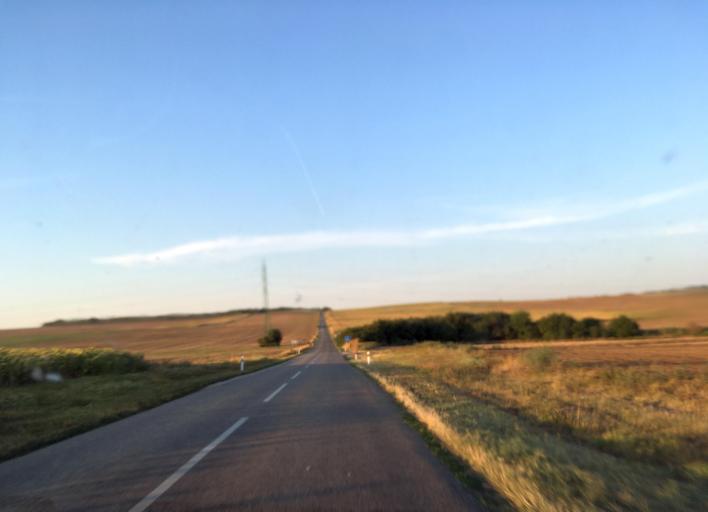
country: SK
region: Nitriansky
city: Svodin
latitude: 47.8508
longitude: 18.4424
